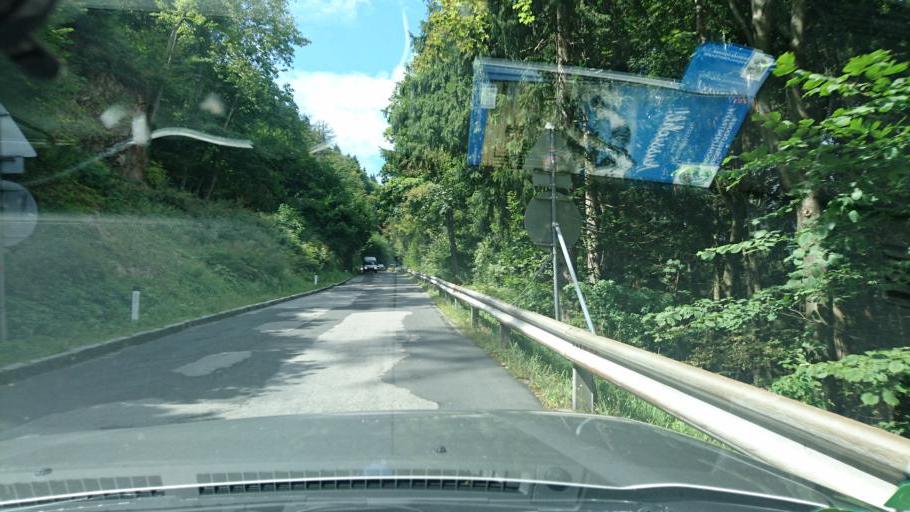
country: AT
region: Carinthia
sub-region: Politischer Bezirk Villach Land
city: Arnoldstein
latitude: 46.5367
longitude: 13.7563
